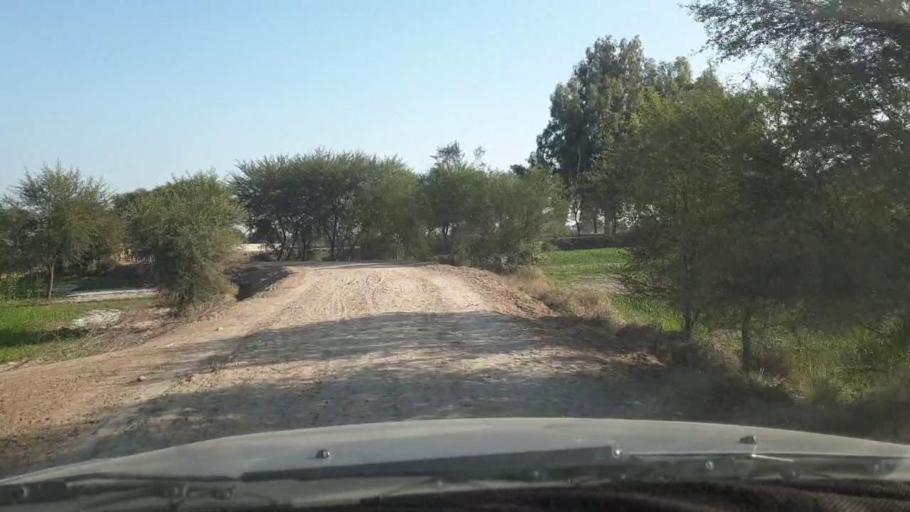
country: PK
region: Sindh
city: Mirpur Mathelo
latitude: 27.9741
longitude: 69.5262
